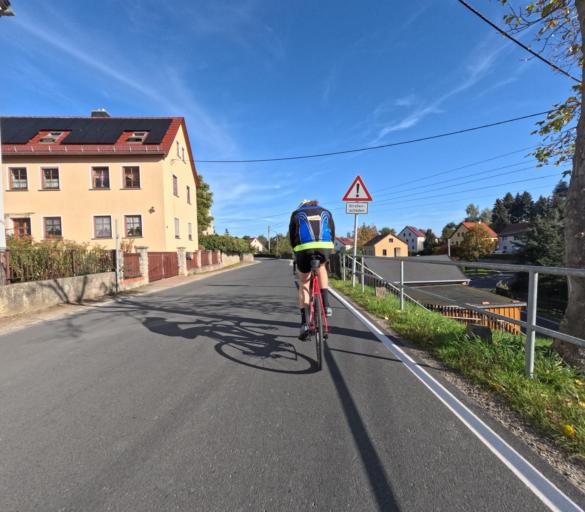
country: DE
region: Saxony
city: Ottendorf-Okrilla
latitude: 51.1351
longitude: 13.8420
